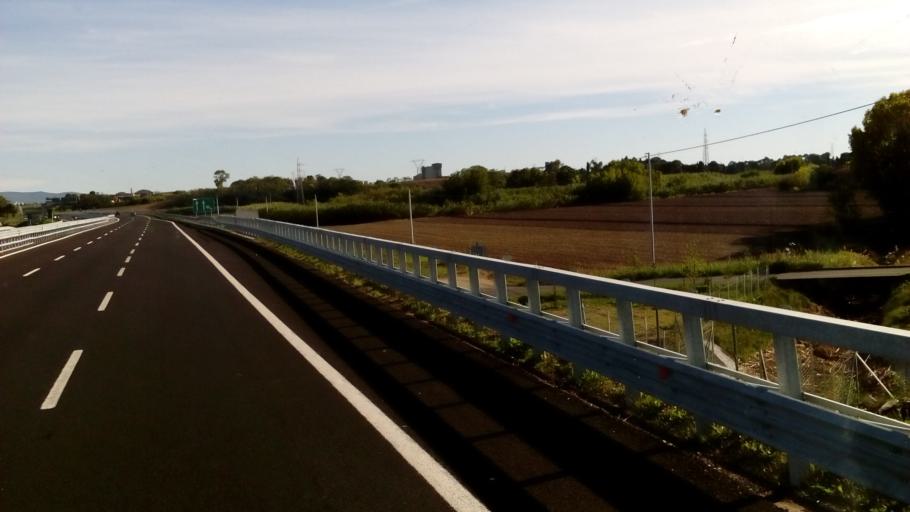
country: IT
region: Latium
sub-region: Provincia di Viterbo
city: Tarquinia
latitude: 42.2541
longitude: 11.7300
